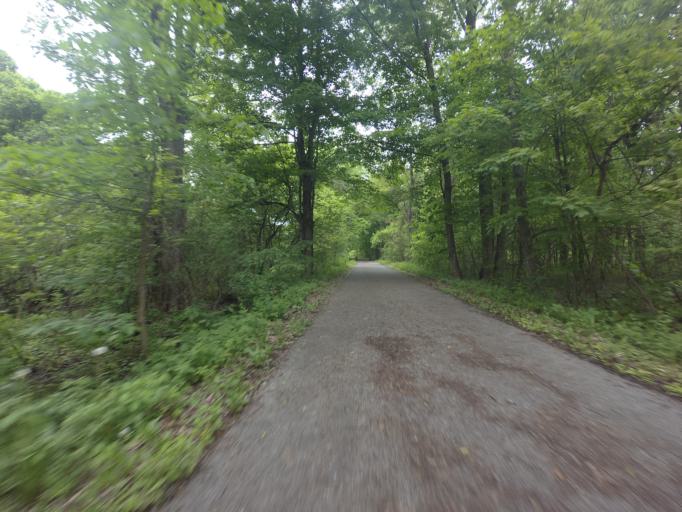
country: US
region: New York
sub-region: Jefferson County
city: Calcium
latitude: 43.9883
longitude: -75.8363
